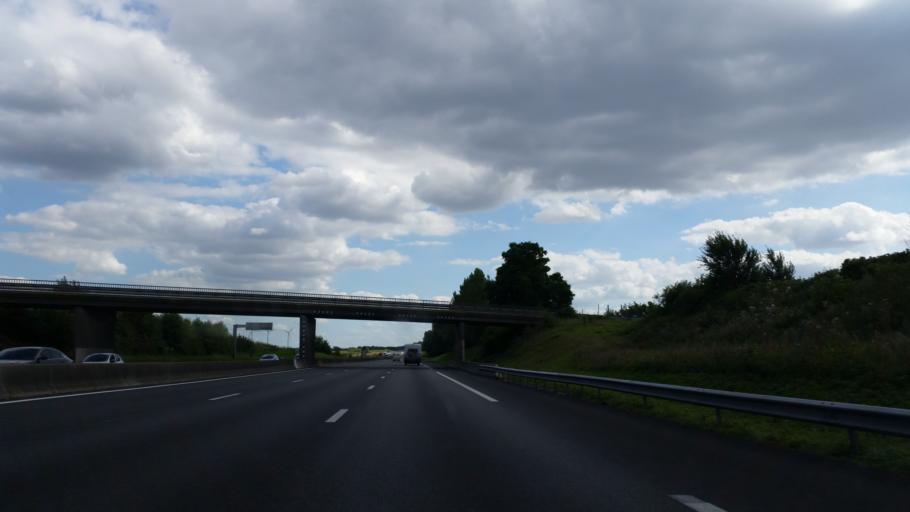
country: FR
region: Nord-Pas-de-Calais
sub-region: Departement du Pas-de-Calais
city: Bapaume
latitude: 50.0726
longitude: 2.8711
